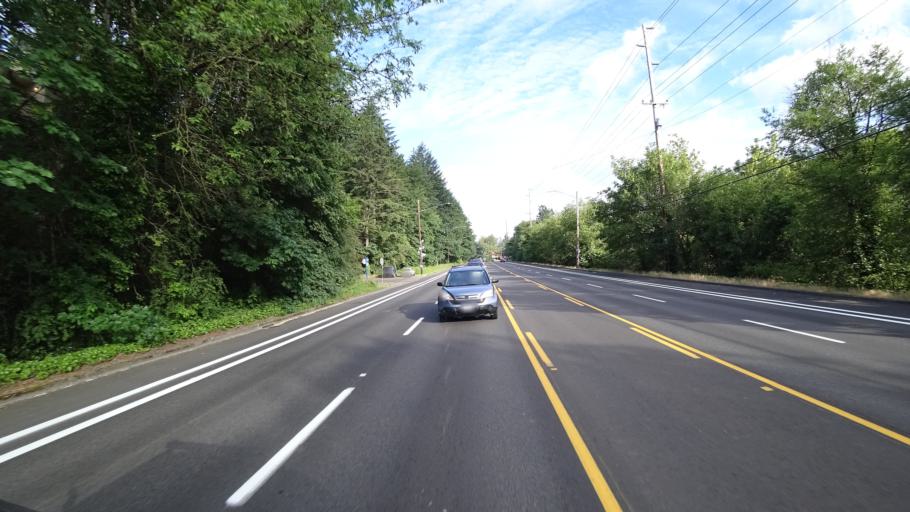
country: US
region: Oregon
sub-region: Washington County
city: Raleigh Hills
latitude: 45.4836
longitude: -122.7145
